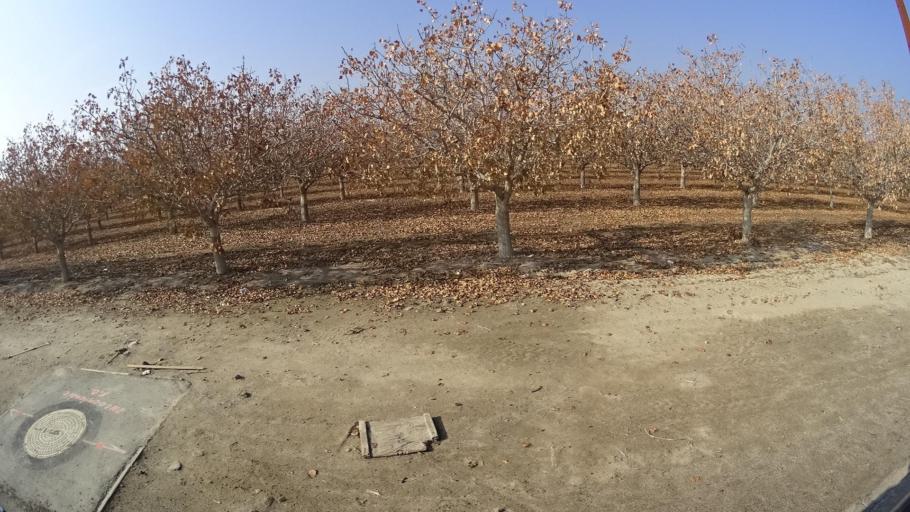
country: US
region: California
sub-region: Kern County
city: Buttonwillow
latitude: 35.4077
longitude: -119.4476
